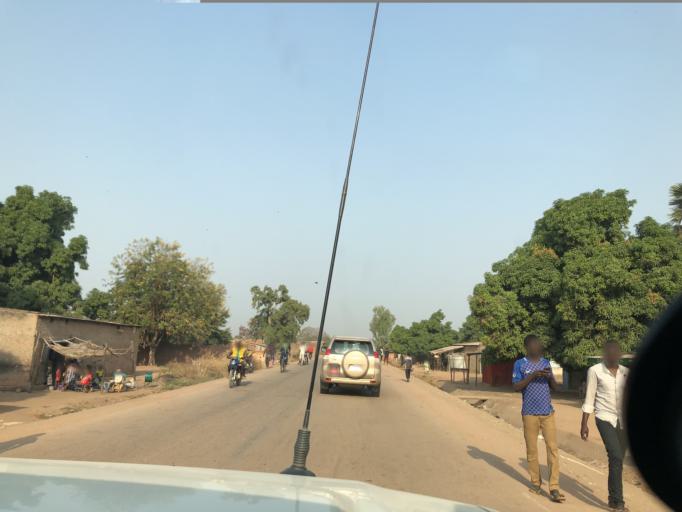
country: TD
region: Logone Occidental
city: Moundou
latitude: 8.5668
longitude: 16.0519
